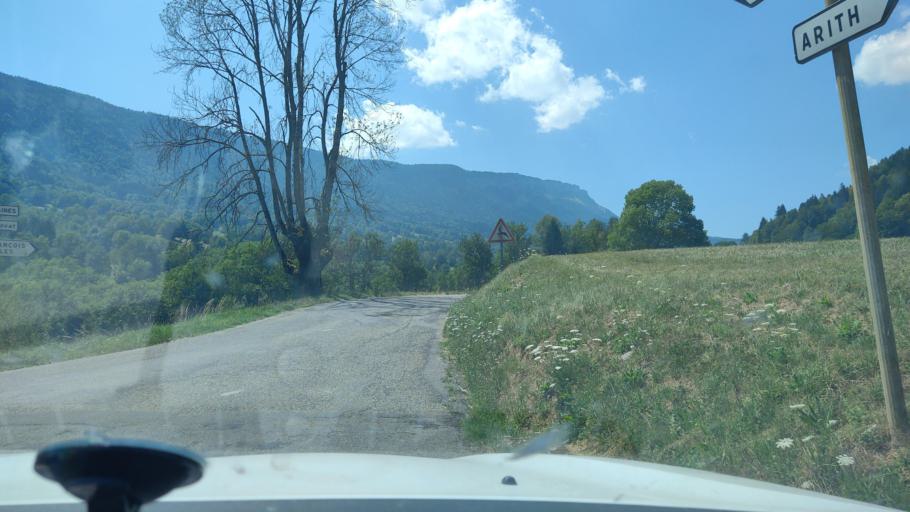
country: FR
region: Rhone-Alpes
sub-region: Departement de la Haute-Savoie
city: Cusy
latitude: 45.6980
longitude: 6.0748
